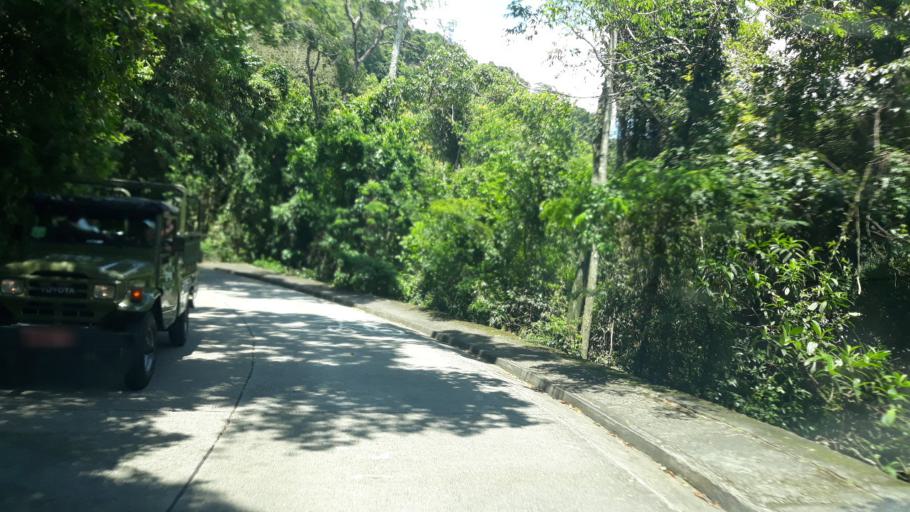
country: BR
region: Rio de Janeiro
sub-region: Rio De Janeiro
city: Rio de Janeiro
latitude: -22.9479
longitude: -43.2105
